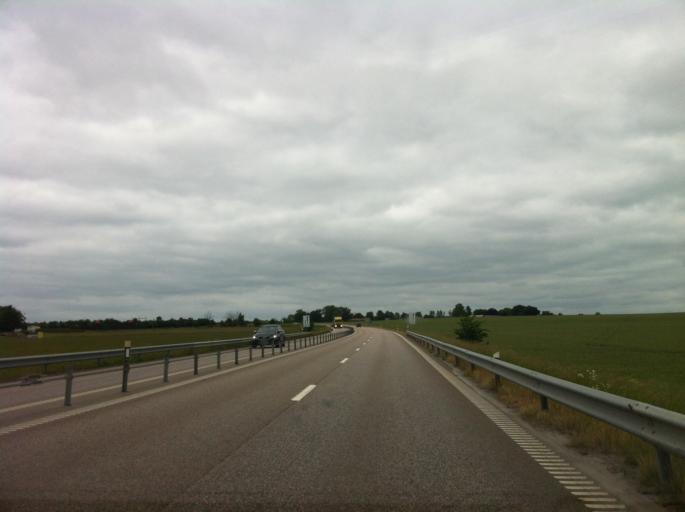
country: SE
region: Skane
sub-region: Eslovs Kommun
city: Eslov
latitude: 55.7963
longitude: 13.3960
